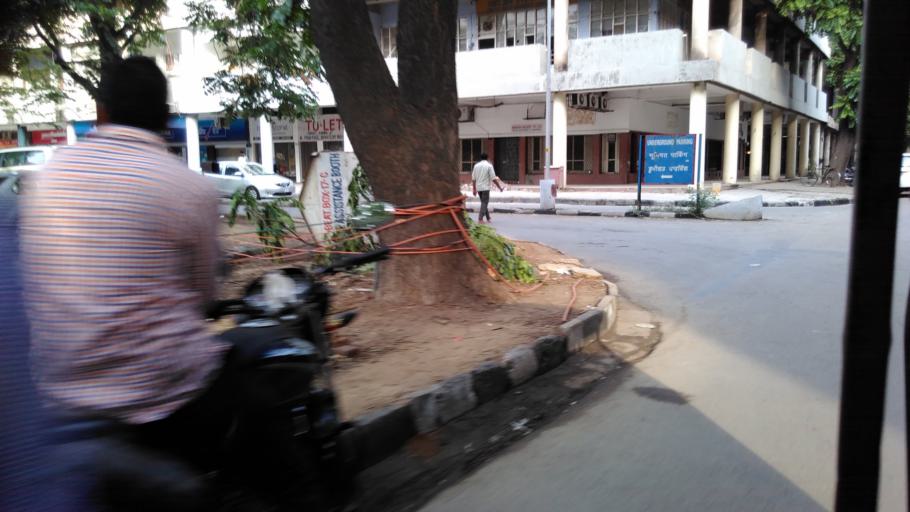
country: IN
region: Chandigarh
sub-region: Chandigarh
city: Chandigarh
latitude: 30.7398
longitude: 76.7842
